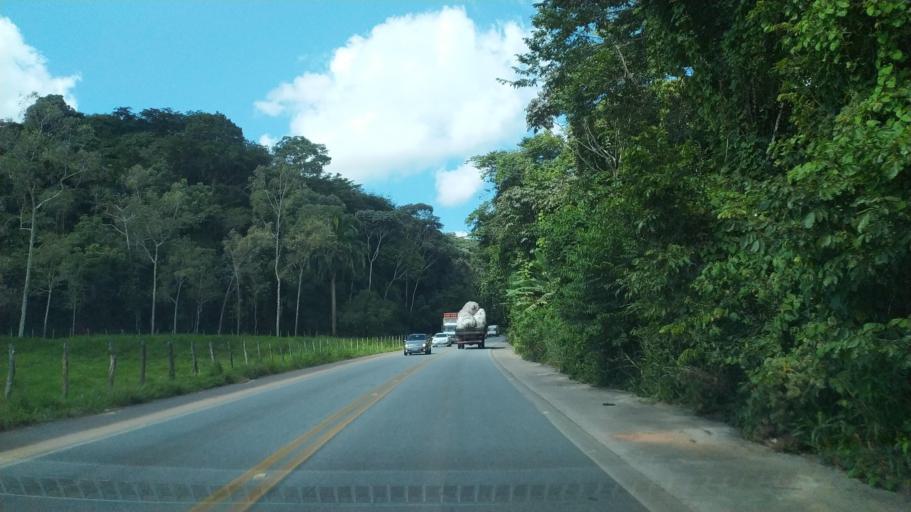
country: BR
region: Alagoas
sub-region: Messias
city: Messias
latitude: -9.3544
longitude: -35.8569
